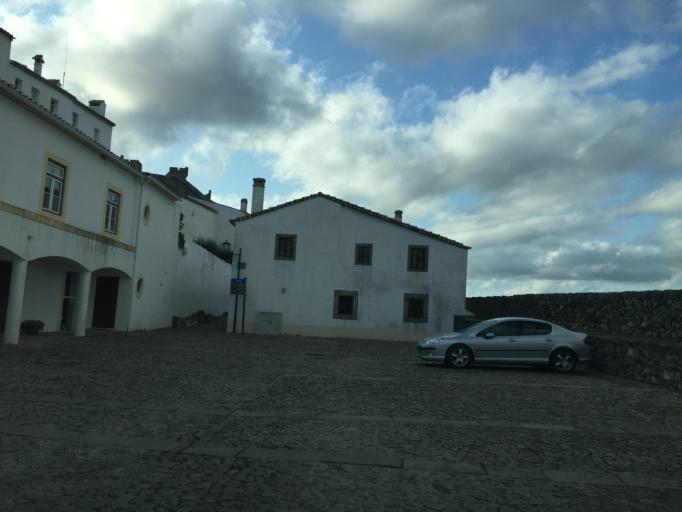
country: PT
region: Portalegre
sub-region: Marvao
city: Marvao
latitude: 39.3947
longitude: -7.3762
